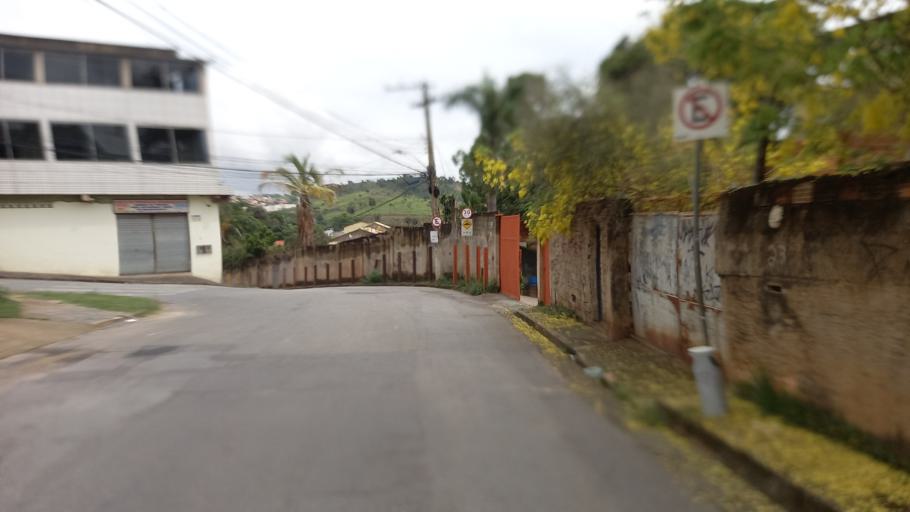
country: BR
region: Minas Gerais
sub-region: Belo Horizonte
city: Belo Horizonte
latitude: -19.9071
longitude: -43.8816
